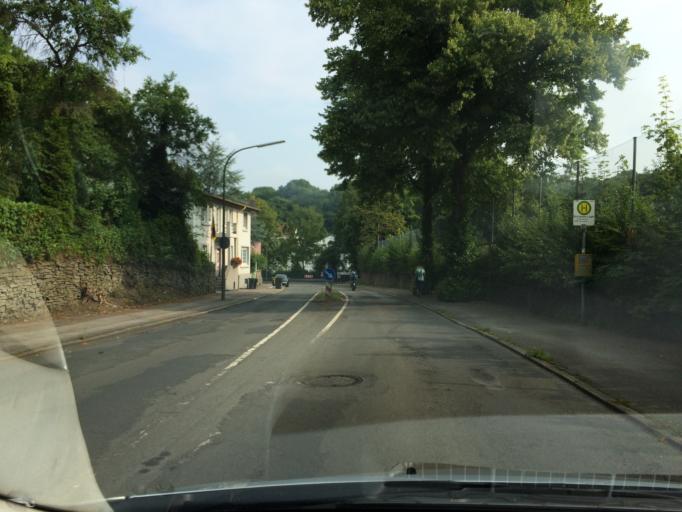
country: DE
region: North Rhine-Westphalia
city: Iserlohn
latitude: 51.3669
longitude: 7.7037
